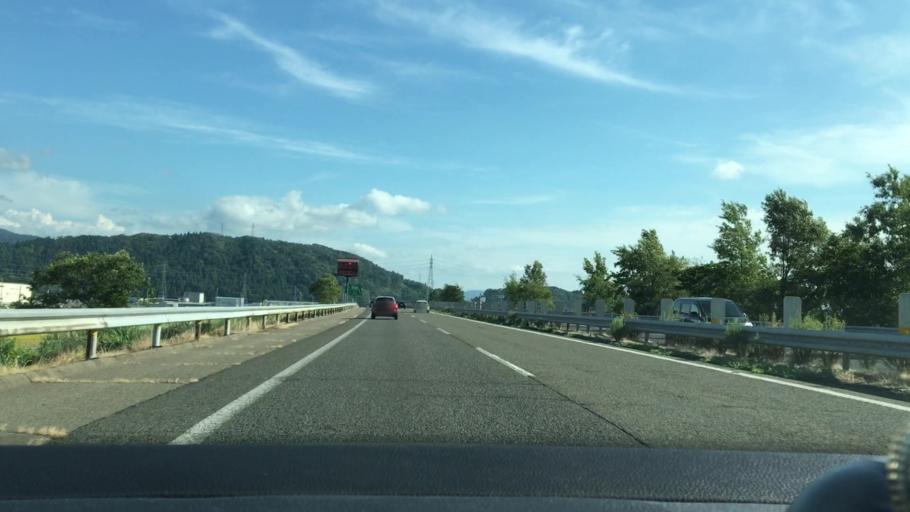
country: JP
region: Fukui
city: Maruoka
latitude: 36.0929
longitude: 136.2784
